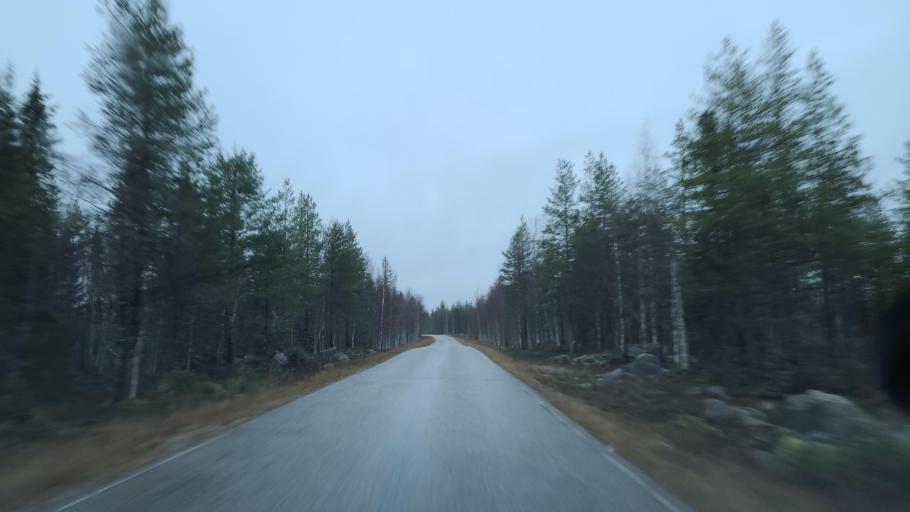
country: FI
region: Lapland
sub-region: Kemi-Tornio
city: Simo
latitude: 65.9229
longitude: 25.2013
